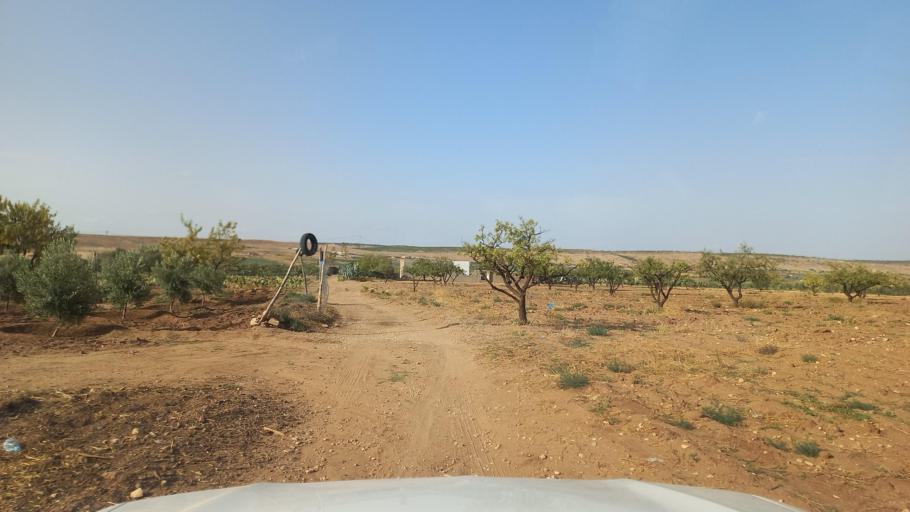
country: TN
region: Al Qasrayn
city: Kasserine
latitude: 35.3453
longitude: 8.8476
